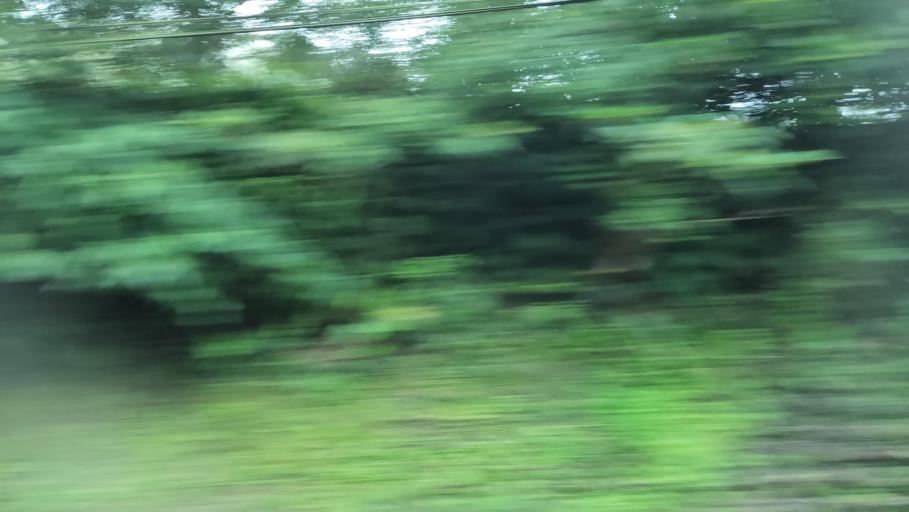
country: TW
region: Taipei
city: Taipei
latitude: 25.1446
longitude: 121.6049
